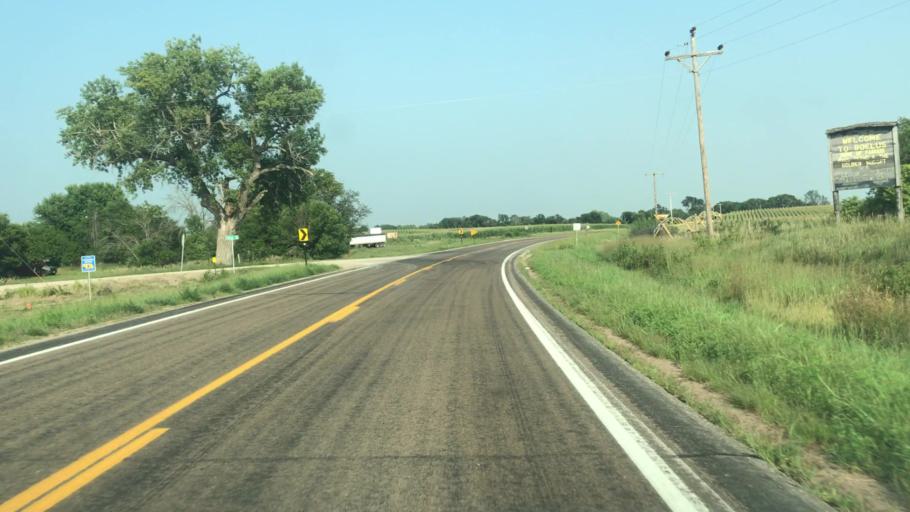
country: US
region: Nebraska
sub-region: Buffalo County
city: Ravenna
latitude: 41.0757
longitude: -98.7303
